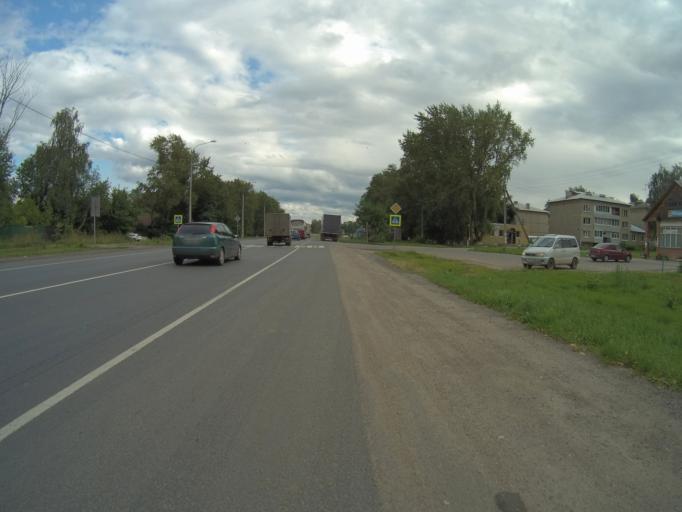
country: RU
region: Vladimir
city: Suzdal'
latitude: 56.3239
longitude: 40.4722
